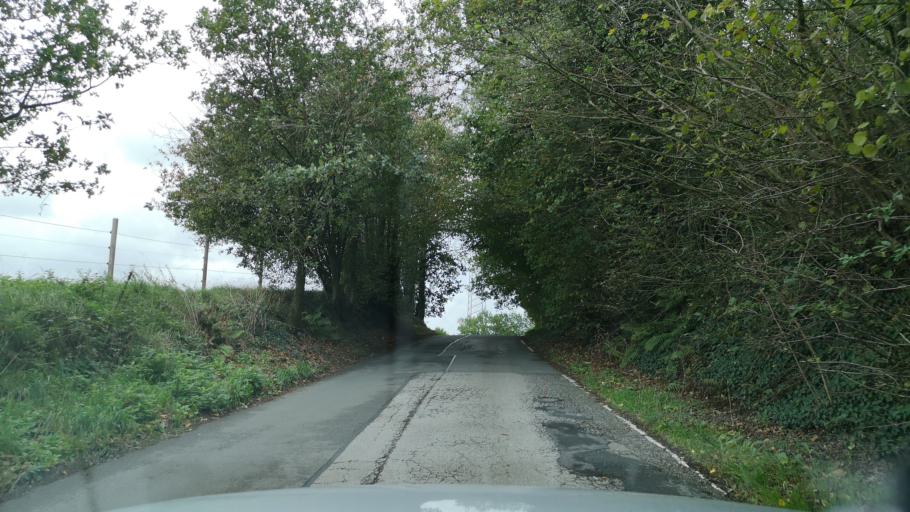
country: DE
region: North Rhine-Westphalia
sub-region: Regierungsbezirk Dusseldorf
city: Velbert
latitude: 51.3711
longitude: 7.0514
